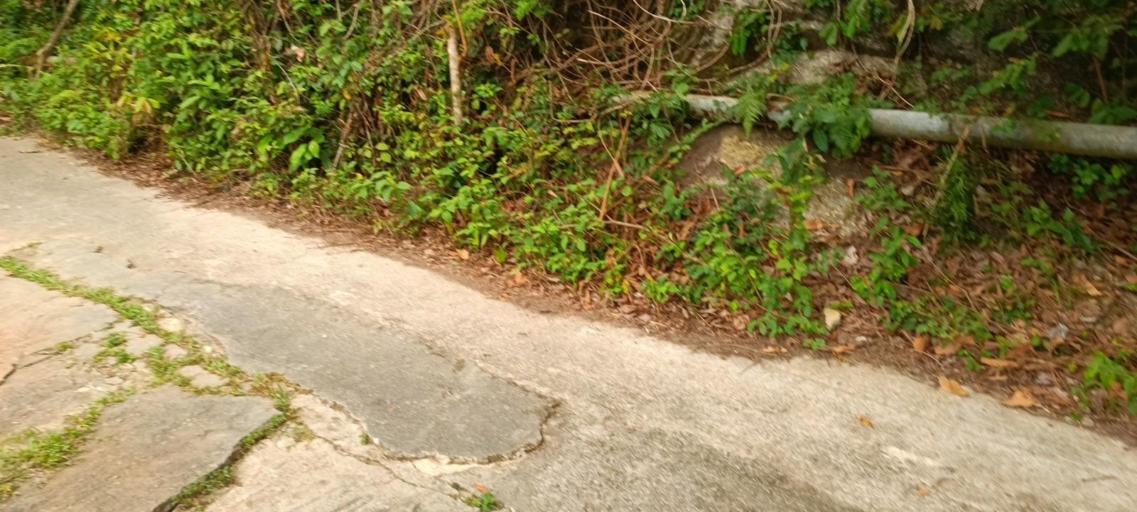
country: MY
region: Penang
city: Juru
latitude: 5.2681
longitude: 100.4156
